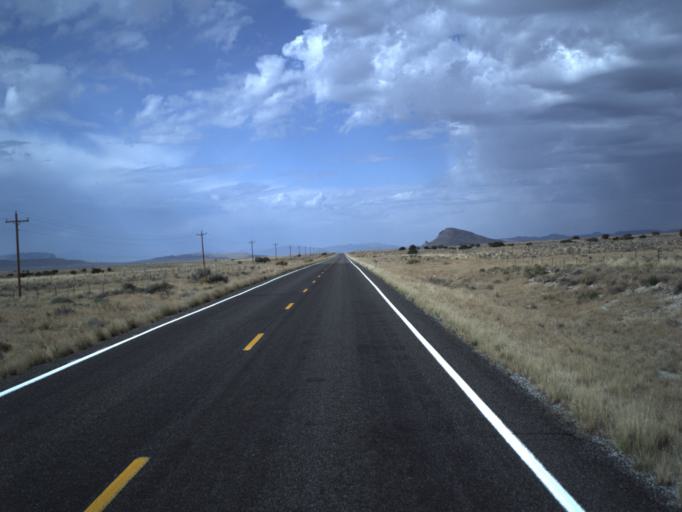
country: US
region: Utah
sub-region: Tooele County
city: Wendover
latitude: 41.4369
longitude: -113.7424
